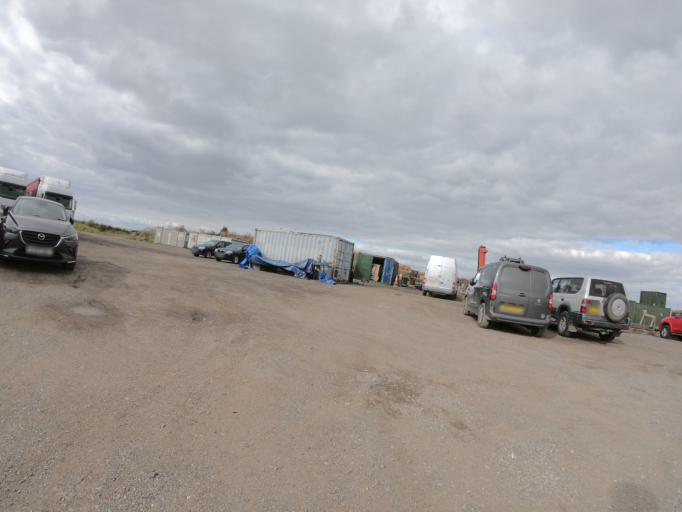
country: GB
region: England
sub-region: Essex
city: Purfleet
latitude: 51.4745
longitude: 0.2231
